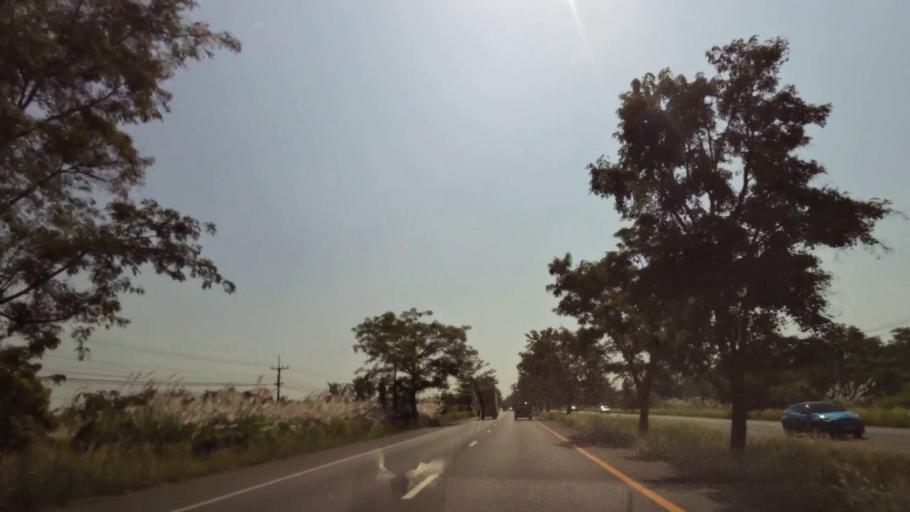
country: TH
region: Nakhon Sawan
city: Kao Liao
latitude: 15.9428
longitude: 100.1141
